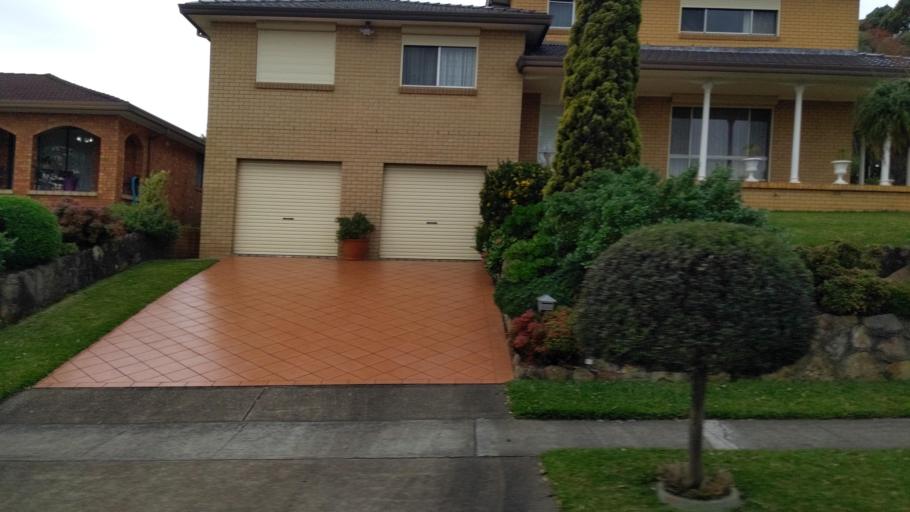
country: AU
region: New South Wales
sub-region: Blacktown
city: Blacktown
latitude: -33.7461
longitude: 150.9299
